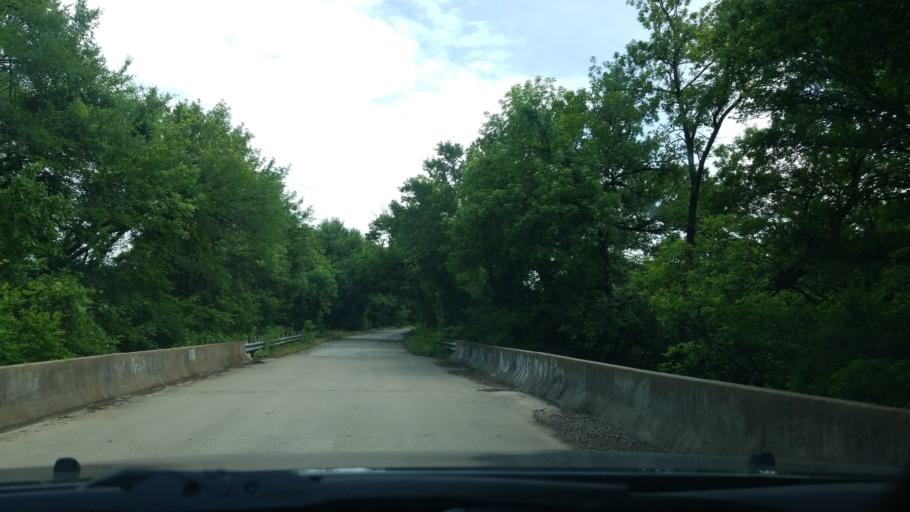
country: US
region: Texas
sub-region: Denton County
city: Sanger
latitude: 33.3149
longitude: -97.1744
